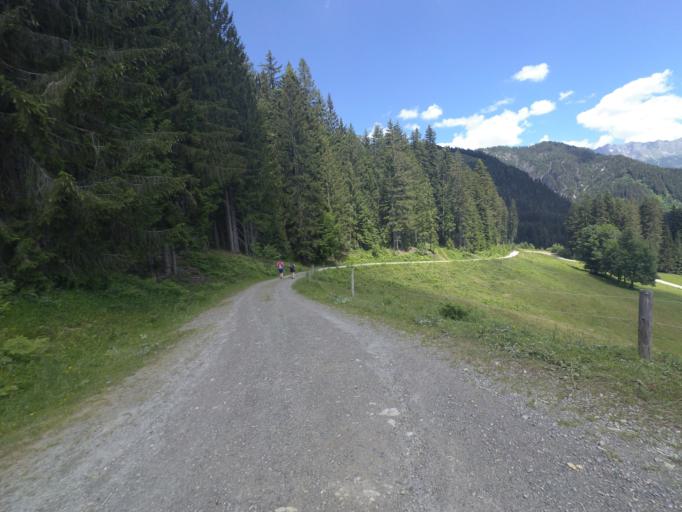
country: AT
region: Salzburg
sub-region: Politischer Bezirk Zell am See
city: Leogang
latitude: 47.4521
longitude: 12.7745
